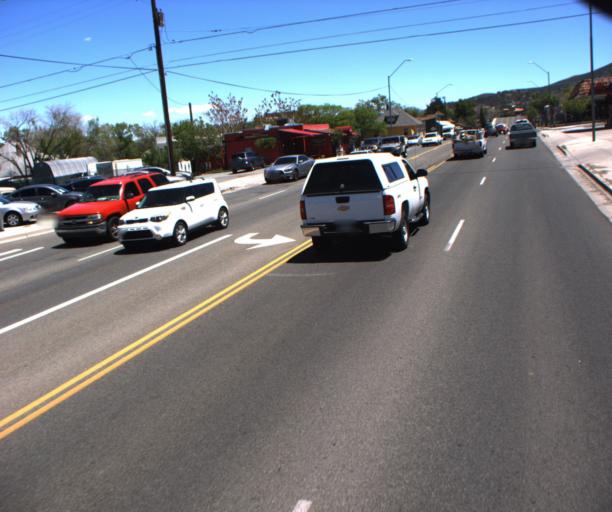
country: US
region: Arizona
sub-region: Yavapai County
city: Prescott
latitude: 34.5453
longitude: -112.4643
